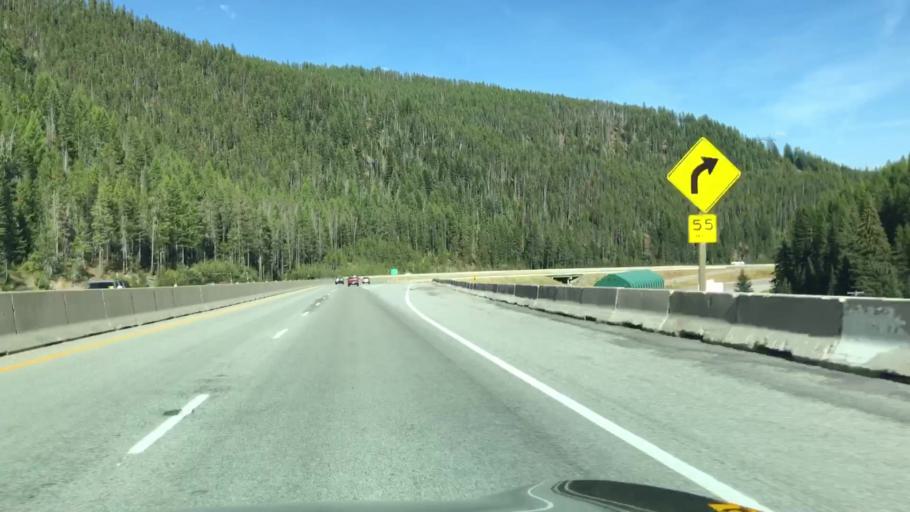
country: US
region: Idaho
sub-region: Shoshone County
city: Wallace
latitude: 47.4208
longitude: -115.6124
